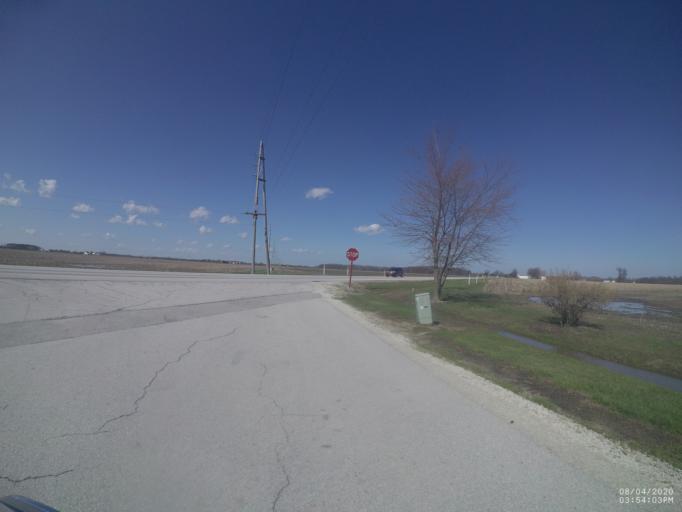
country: US
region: Ohio
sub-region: Sandusky County
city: Ballville
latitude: 41.2810
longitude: -83.1880
